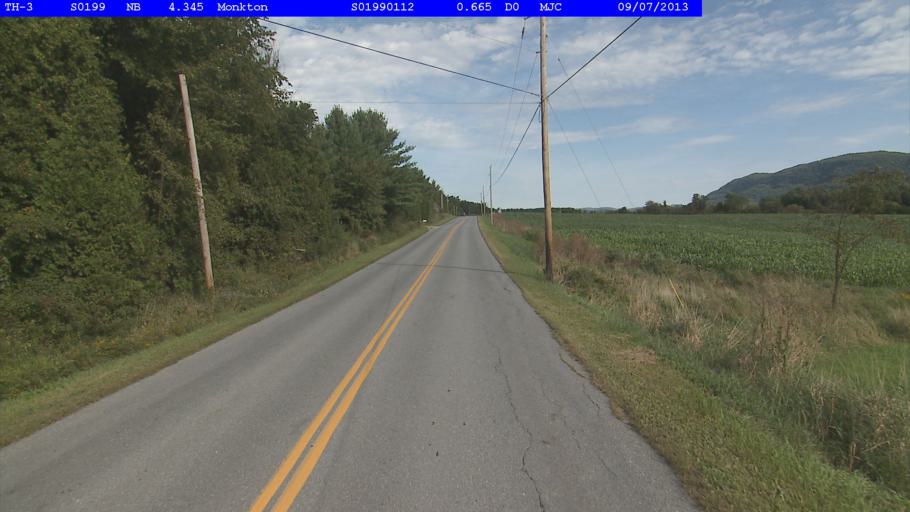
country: US
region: Vermont
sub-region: Addison County
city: Bristol
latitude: 44.1902
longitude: -73.1084
